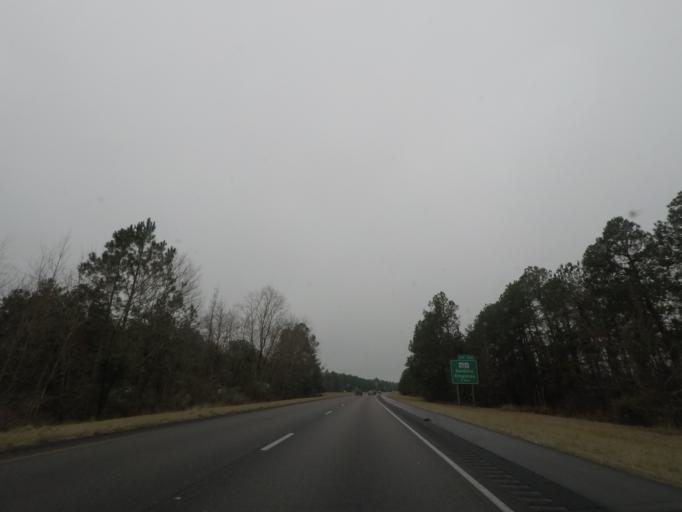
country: US
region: South Carolina
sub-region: Sumter County
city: East Sumter
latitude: 33.8753
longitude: -80.1031
